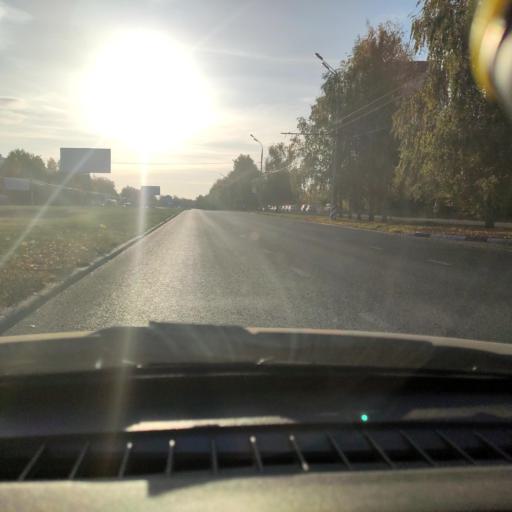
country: RU
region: Samara
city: Tol'yatti
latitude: 53.5036
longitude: 49.2584
